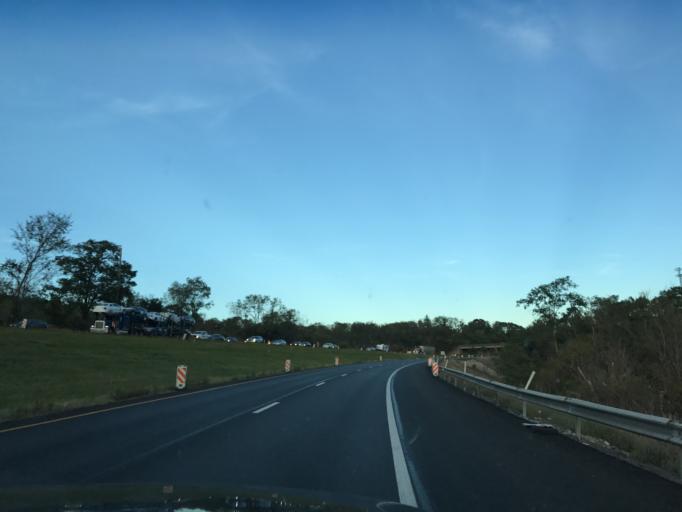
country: US
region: Pennsylvania
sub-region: Washington County
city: Wolfdale
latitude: 40.1305
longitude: -80.3562
